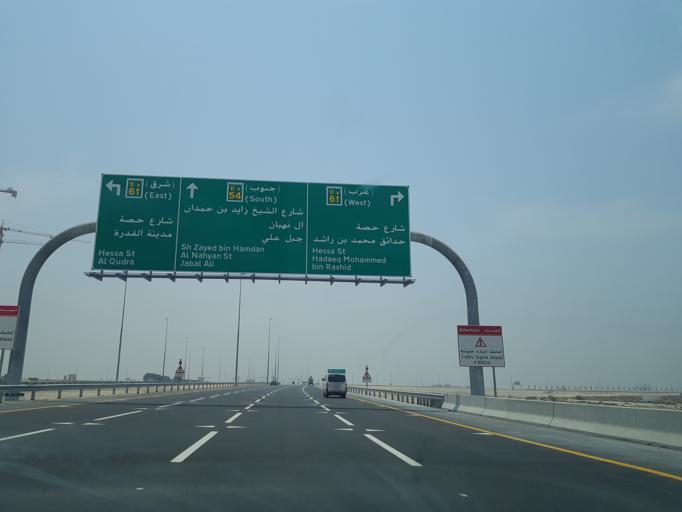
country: AE
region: Dubai
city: Dubai
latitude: 25.0273
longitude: 55.2448
